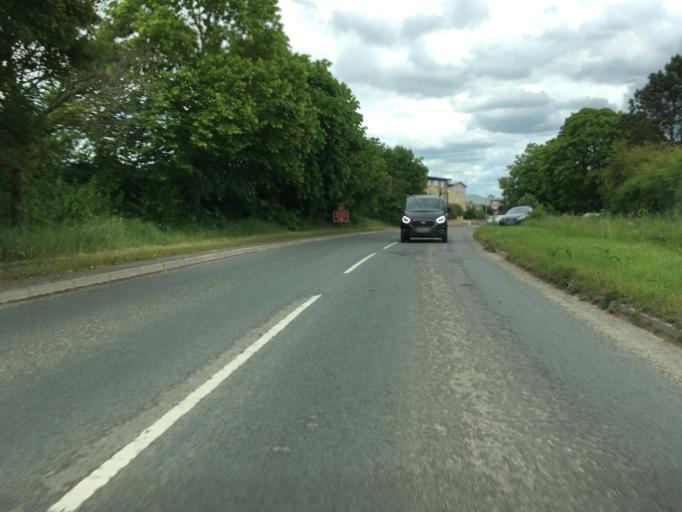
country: GB
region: England
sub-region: Gloucestershire
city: Cirencester
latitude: 51.7024
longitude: -1.9636
